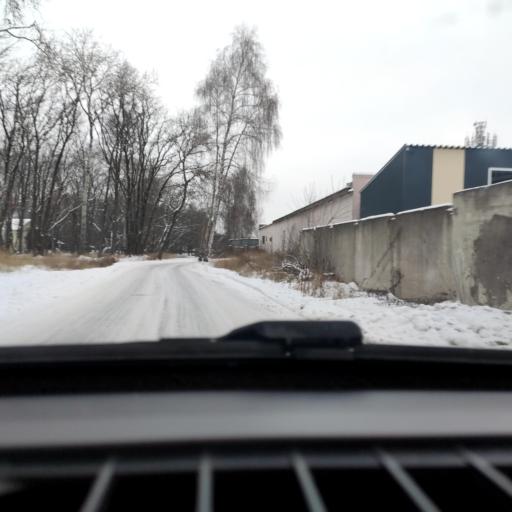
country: RU
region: Voronezj
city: Podgornoye
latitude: 51.7867
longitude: 39.1624
